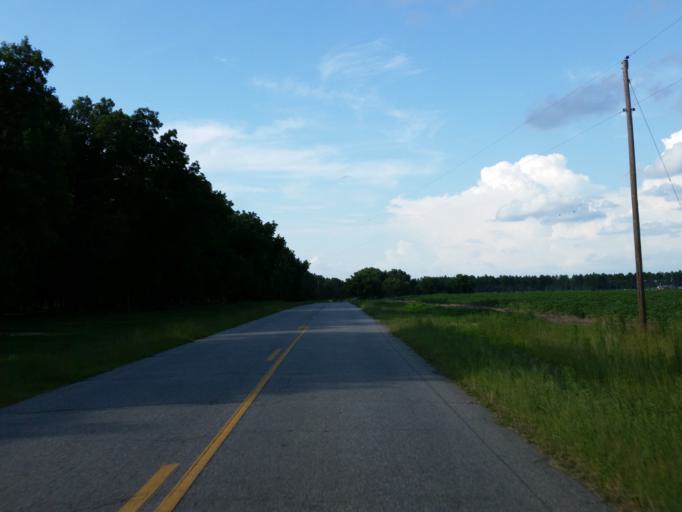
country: US
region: Georgia
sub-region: Dooly County
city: Vienna
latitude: 32.0517
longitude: -83.8295
